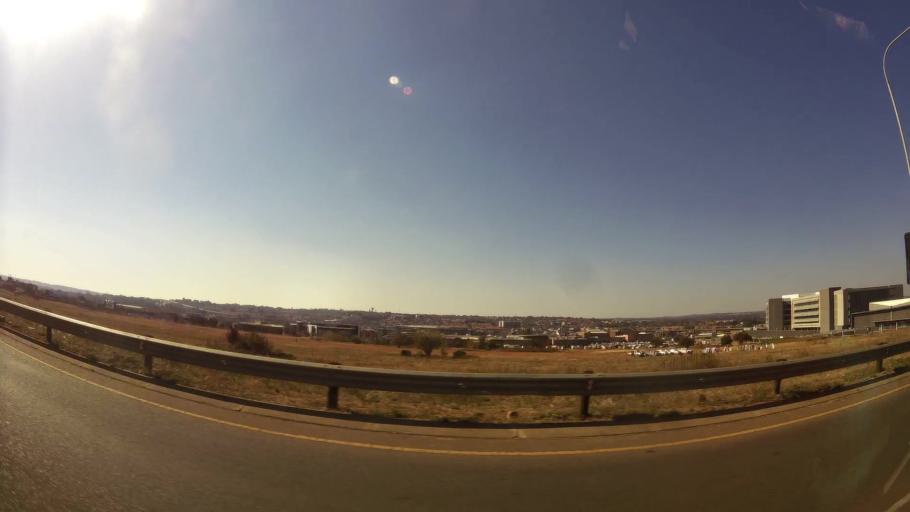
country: ZA
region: Gauteng
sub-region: City of Tshwane Metropolitan Municipality
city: Centurion
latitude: -25.8608
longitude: 28.1820
